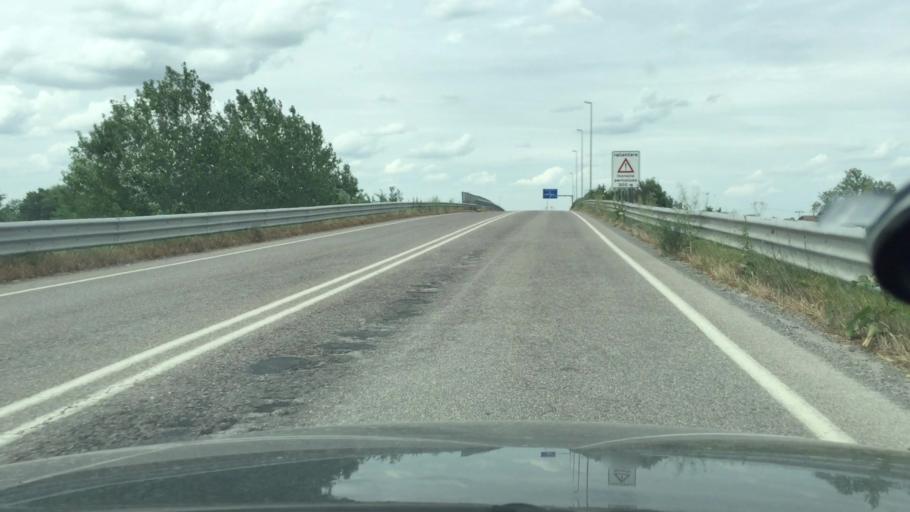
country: IT
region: Emilia-Romagna
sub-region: Provincia di Ferrara
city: Cona
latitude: 44.8017
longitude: 11.7214
